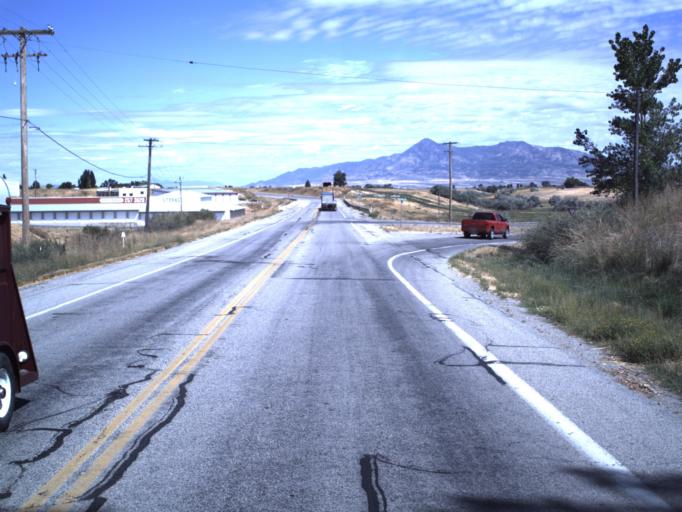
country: US
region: Utah
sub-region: Box Elder County
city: Garland
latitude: 41.7393
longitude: -112.1436
